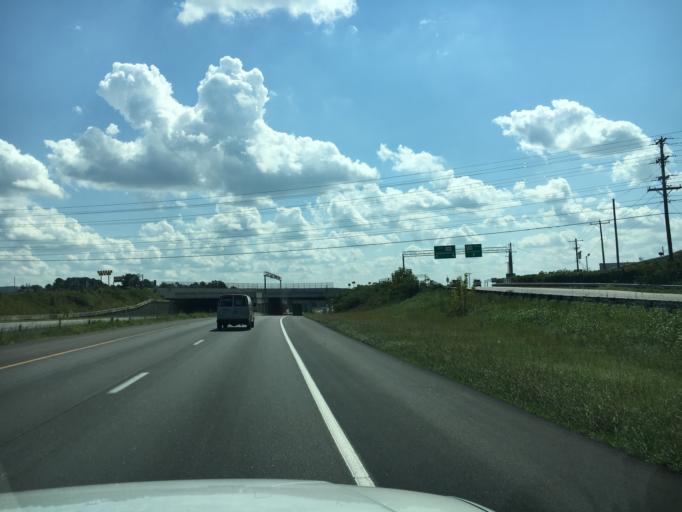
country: US
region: South Carolina
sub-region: Spartanburg County
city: Arcadia
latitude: 34.9245
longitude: -81.9890
